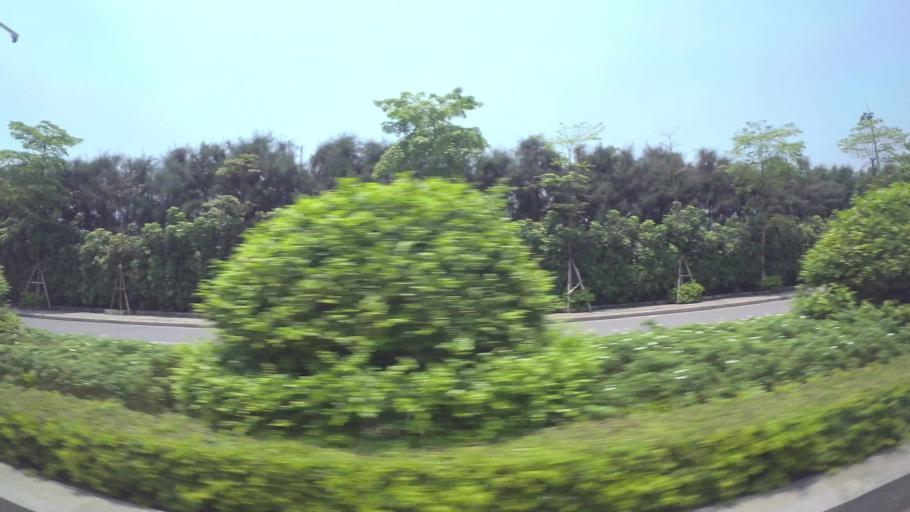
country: VN
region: Ha Noi
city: Trau Quy
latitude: 21.0366
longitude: 105.8966
